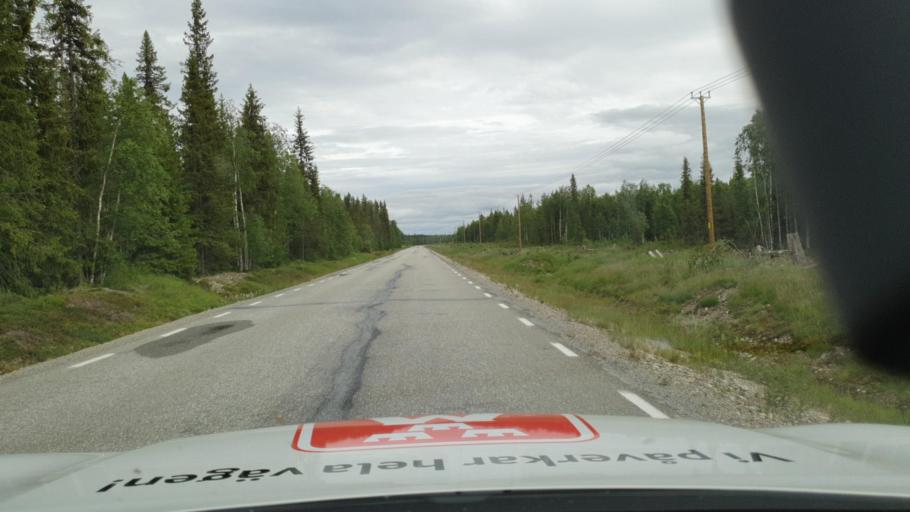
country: SE
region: Vaesterbotten
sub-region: Lycksele Kommun
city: Soderfors
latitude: 64.3715
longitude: 18.0648
